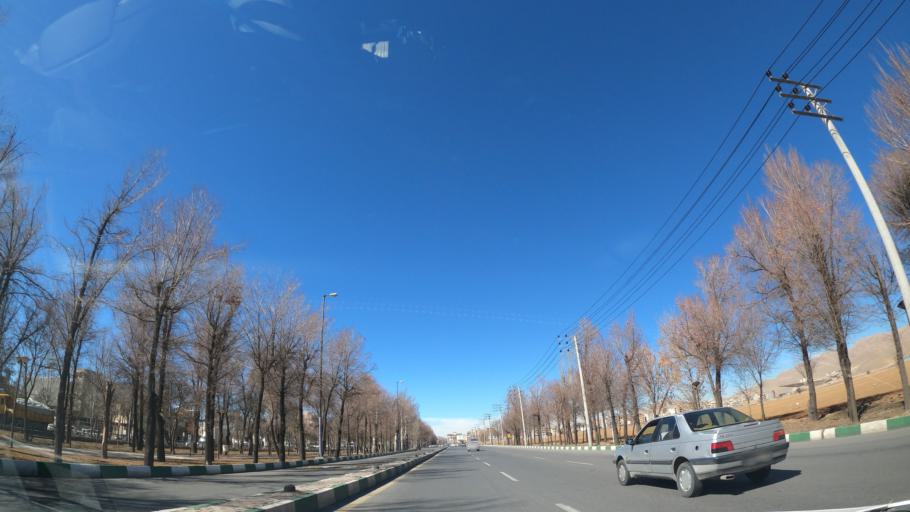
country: IR
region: Chahar Mahall va Bakhtiari
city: Shahrekord
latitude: 32.3092
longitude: 50.8954
